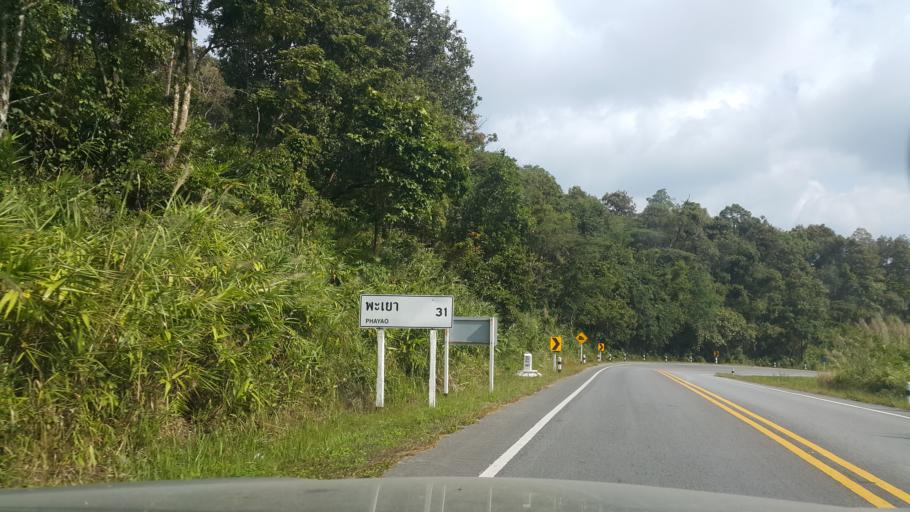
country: TH
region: Phayao
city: Phayao
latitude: 19.0632
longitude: 99.7731
